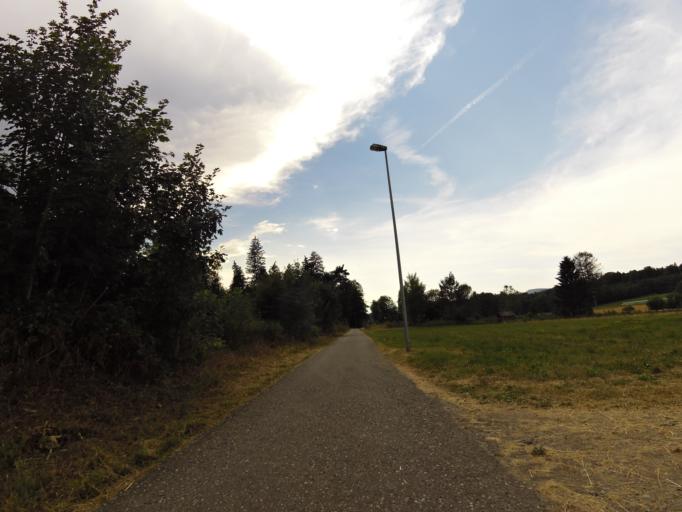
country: CH
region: Aargau
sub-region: Bezirk Aarau
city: Buchs
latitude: 47.3822
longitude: 8.0995
